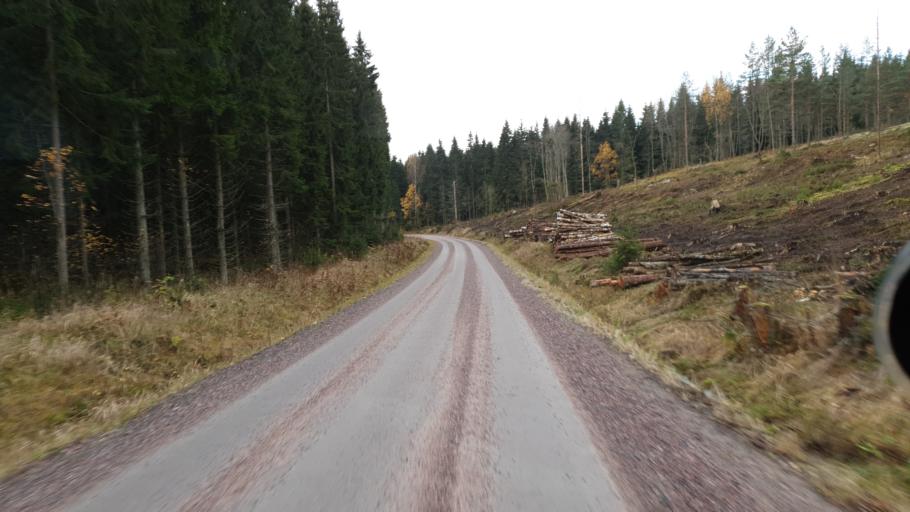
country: FI
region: Uusimaa
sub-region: Helsinki
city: Siuntio
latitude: 60.1537
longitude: 24.2781
